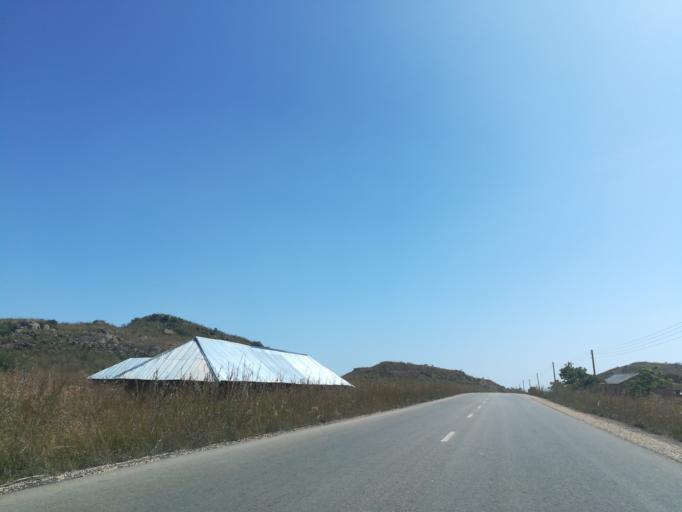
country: NG
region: Plateau
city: Bukuru
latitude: 9.7741
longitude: 8.9181
